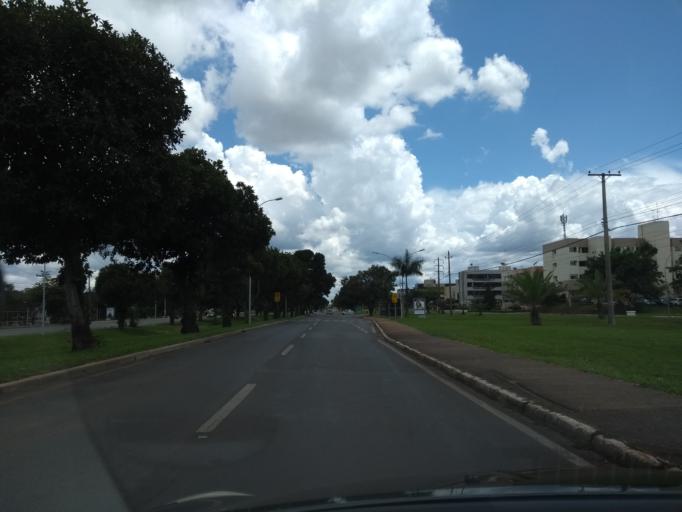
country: BR
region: Federal District
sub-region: Brasilia
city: Brasilia
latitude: -15.7915
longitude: -47.9330
